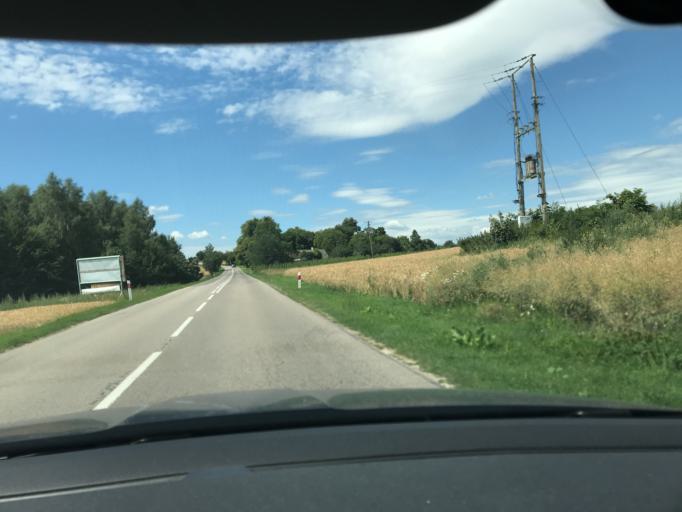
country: PL
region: Lublin Voivodeship
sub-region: Powiat zamojski
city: Szczebrzeszyn
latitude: 50.7133
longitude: 22.9163
